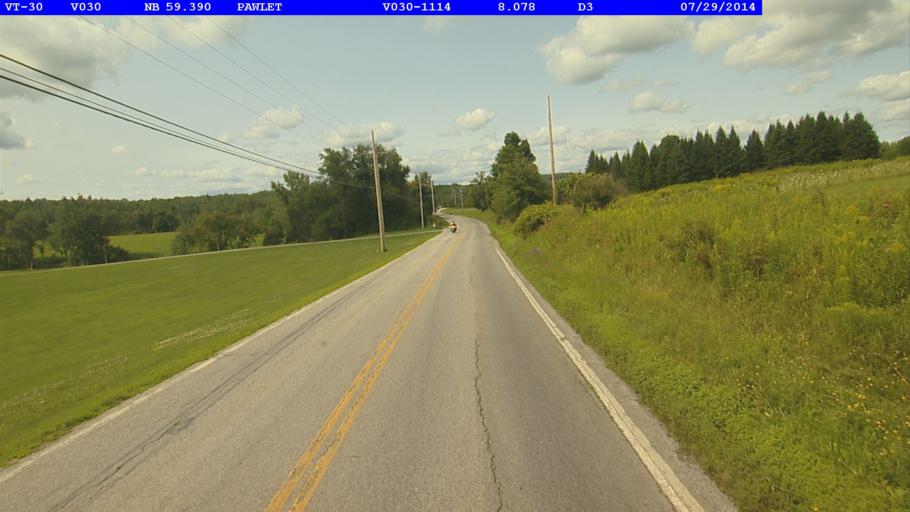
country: US
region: New York
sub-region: Washington County
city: Granville
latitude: 43.4052
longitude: -73.2256
